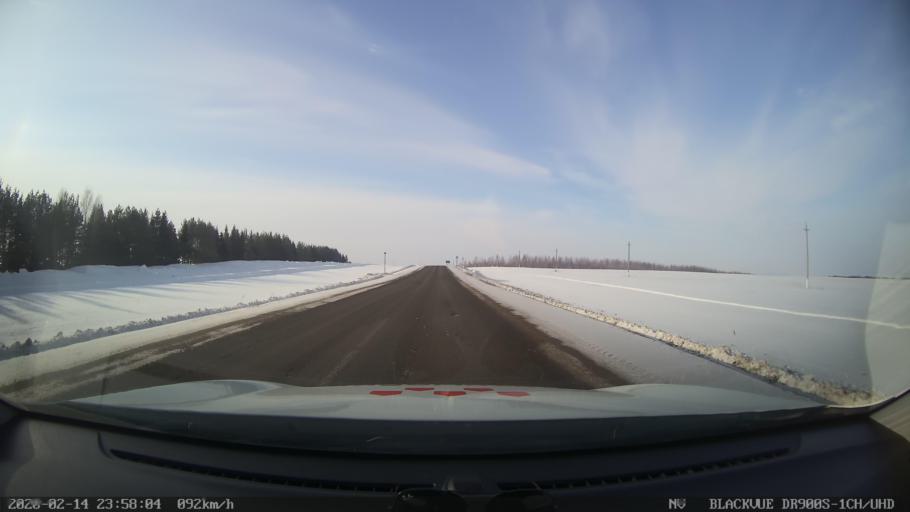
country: RU
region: Tatarstan
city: Kuybyshevskiy Zaton
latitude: 55.3381
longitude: 49.0958
